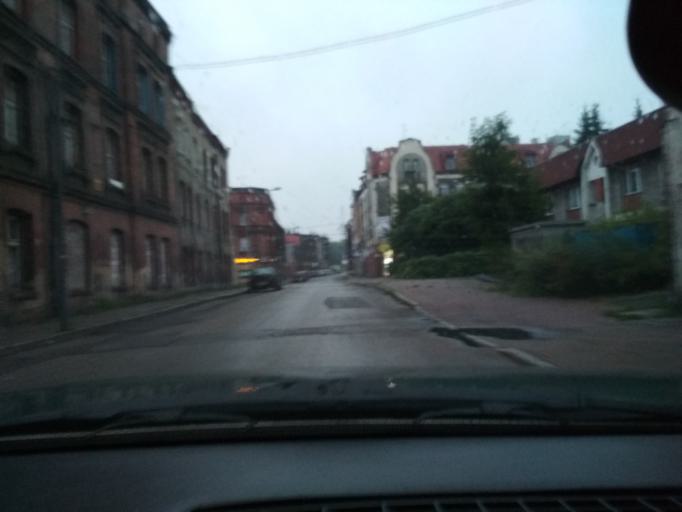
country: PL
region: Silesian Voivodeship
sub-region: Swietochlowice
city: Swietochlowice
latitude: 50.2919
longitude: 18.9208
